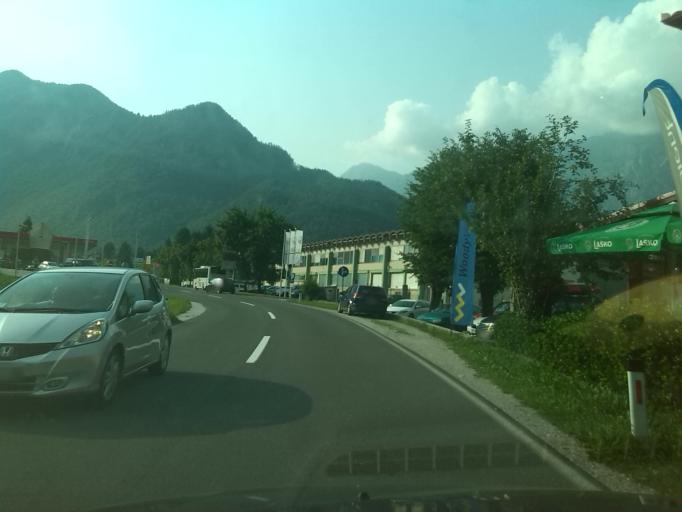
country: SI
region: Kobarid
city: Kobarid
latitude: 46.2411
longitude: 13.5835
